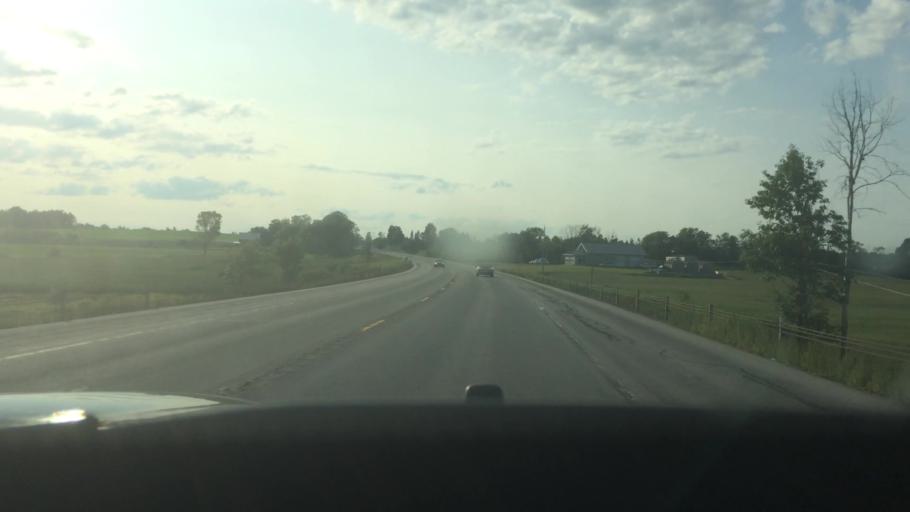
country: US
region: New York
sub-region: St. Lawrence County
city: Canton
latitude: 44.6307
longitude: -75.2433
